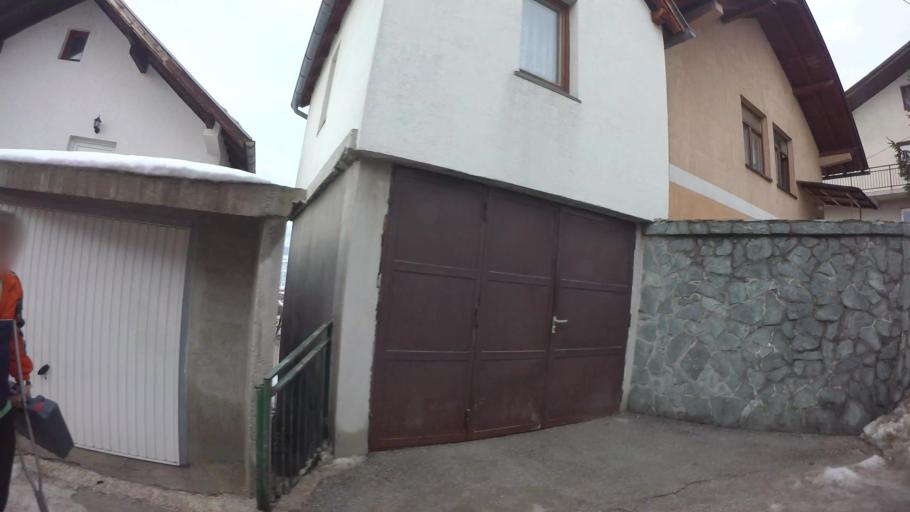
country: BA
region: Federation of Bosnia and Herzegovina
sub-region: Kanton Sarajevo
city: Sarajevo
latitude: 43.8644
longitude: 18.3300
